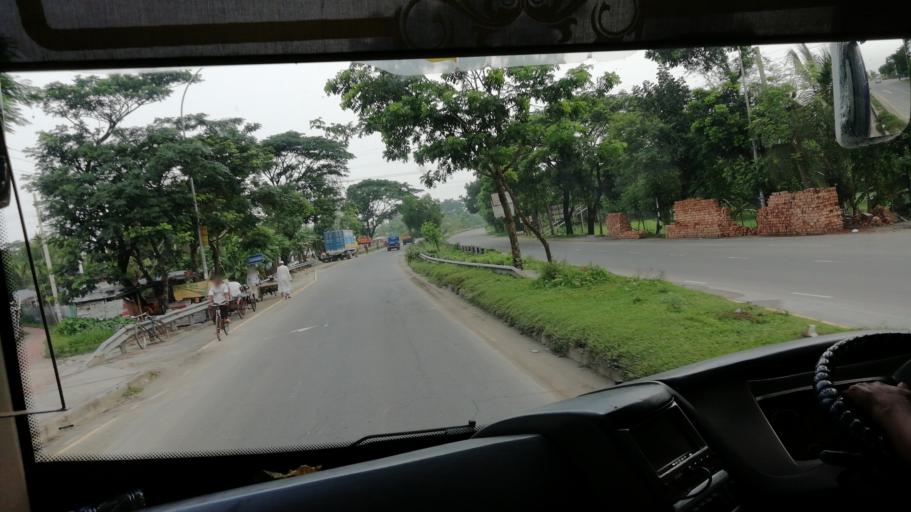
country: BD
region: Khulna
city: Khulna
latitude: 22.7864
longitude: 89.5362
